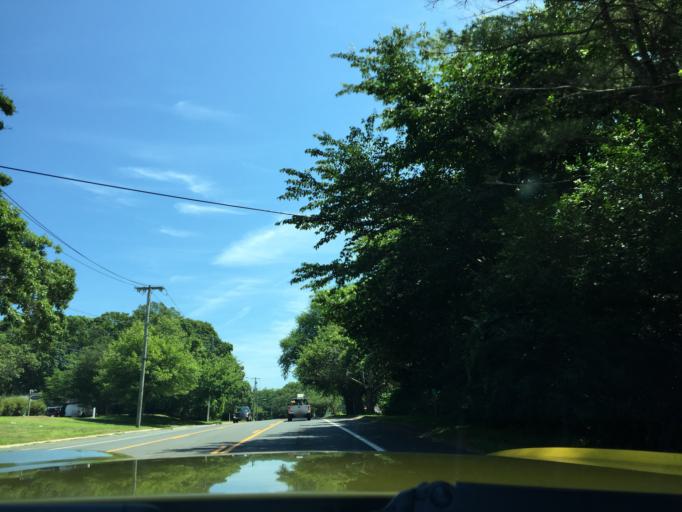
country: US
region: New York
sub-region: Suffolk County
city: Amagansett
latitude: 40.9698
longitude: -72.1580
